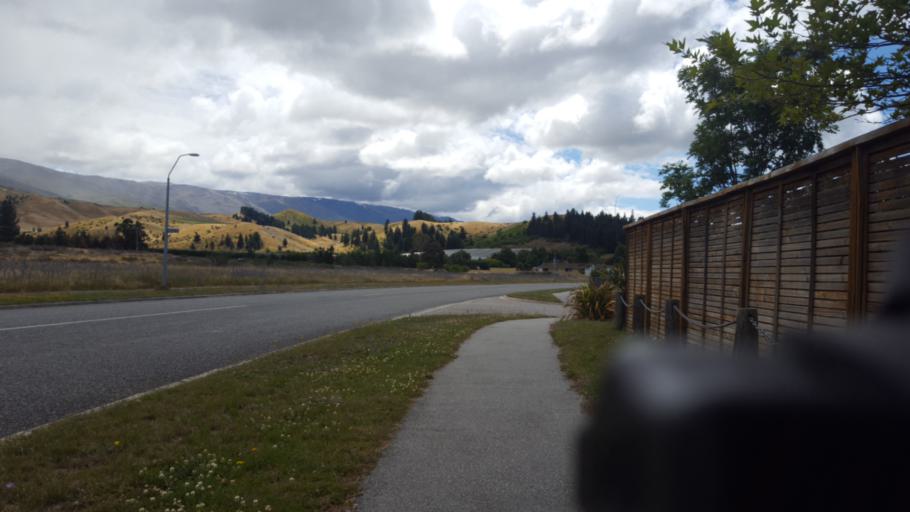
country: NZ
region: Otago
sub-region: Queenstown-Lakes District
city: Wanaka
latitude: -45.0429
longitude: 169.1799
